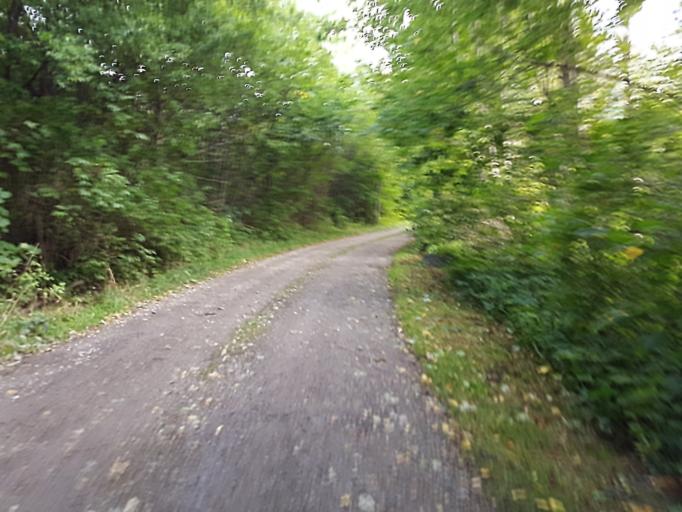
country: DK
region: Zealand
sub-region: Roskilde Kommune
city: Gundsomagle
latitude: 55.7494
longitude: 12.1365
